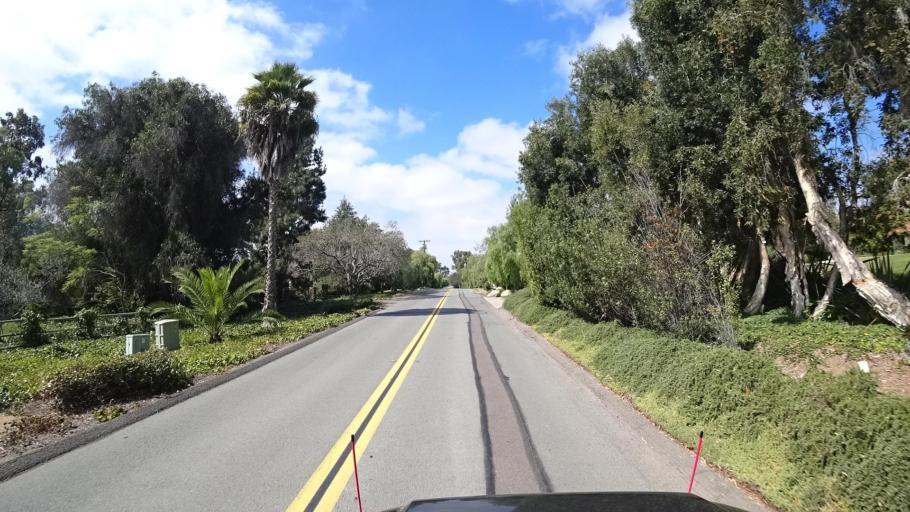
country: US
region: California
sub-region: San Diego County
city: Rancho Santa Fe
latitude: 33.0255
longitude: -117.2063
